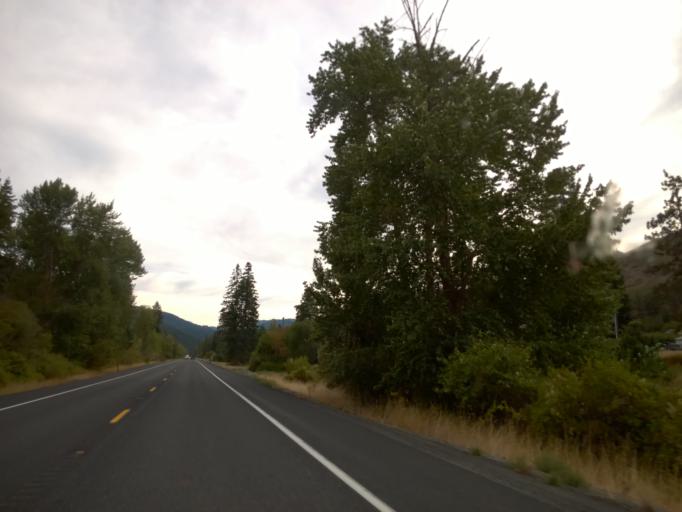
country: US
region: Washington
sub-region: Chelan County
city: Leavenworth
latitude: 47.5341
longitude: -120.6211
